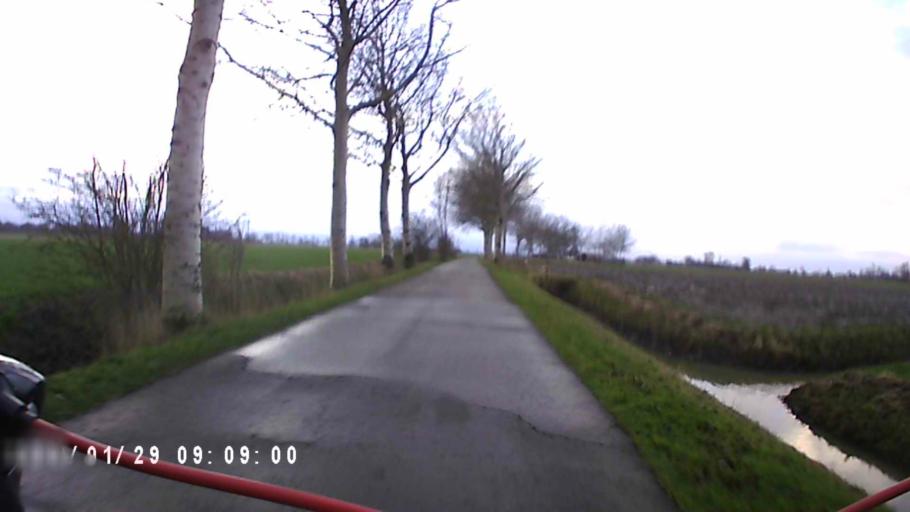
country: NL
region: Groningen
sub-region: Gemeente Zuidhorn
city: Aduard
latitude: 53.3136
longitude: 6.4551
